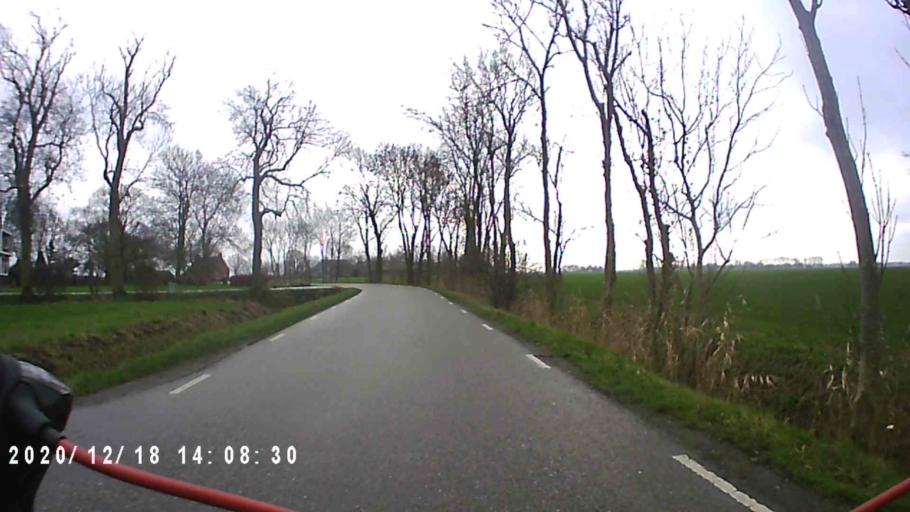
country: NL
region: Groningen
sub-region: Gemeente Bedum
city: Bedum
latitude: 53.2817
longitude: 6.6571
